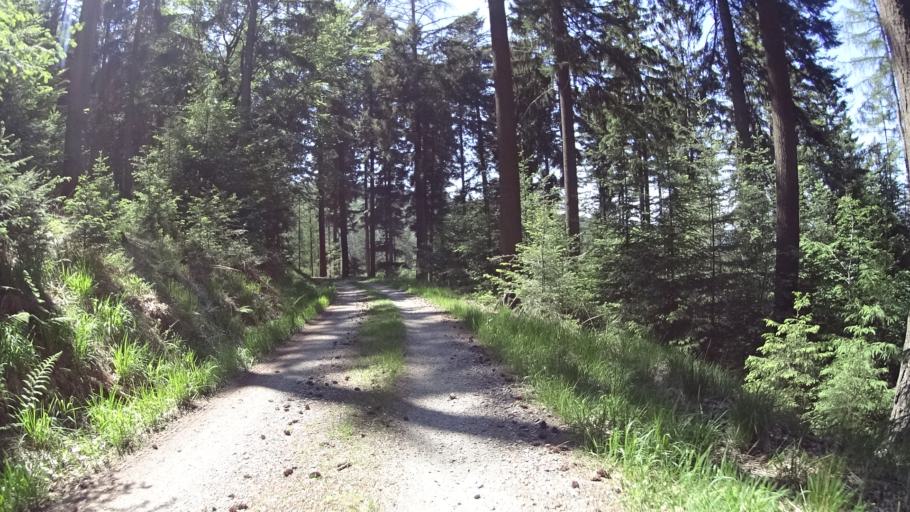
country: DE
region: Baden-Wuerttemberg
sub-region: Karlsruhe Region
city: Wilhelmsfeld
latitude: 49.4592
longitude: 8.7236
